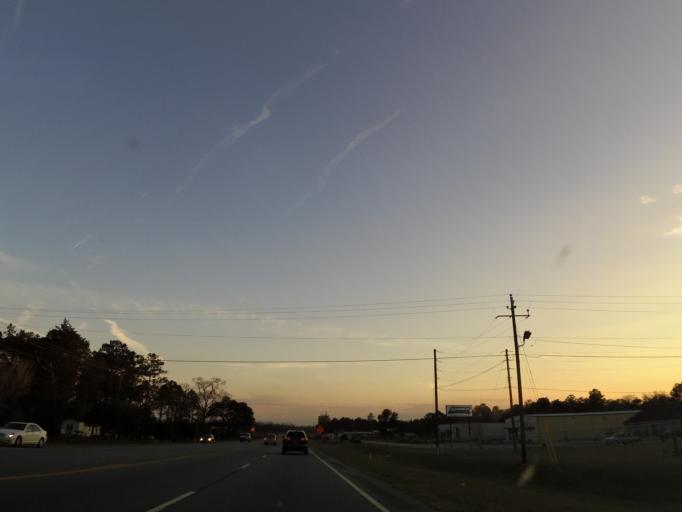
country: US
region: Georgia
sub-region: Lee County
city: Leesburg
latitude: 31.6621
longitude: -84.1729
